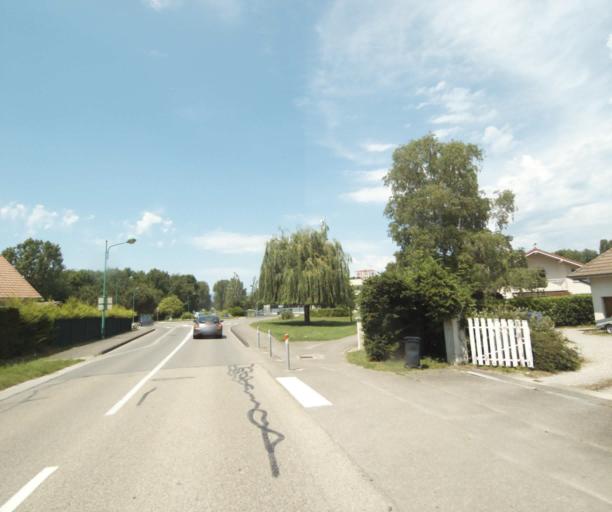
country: FR
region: Rhone-Alpes
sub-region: Departement de la Haute-Savoie
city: Douvaine
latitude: 46.3113
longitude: 6.3010
